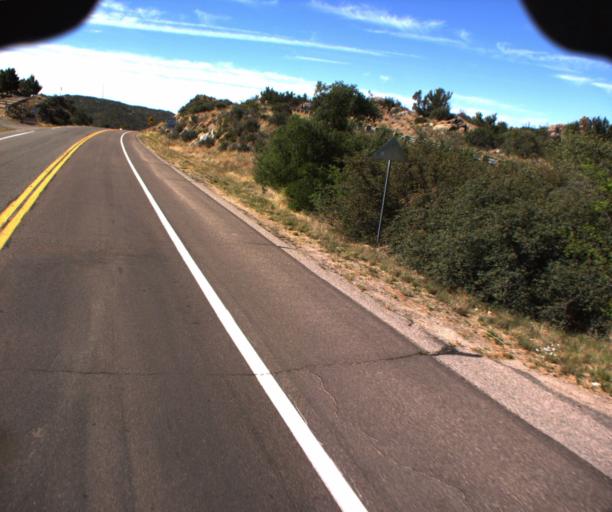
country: US
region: Arizona
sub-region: Yavapai County
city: Congress
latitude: 34.2121
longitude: -112.7554
